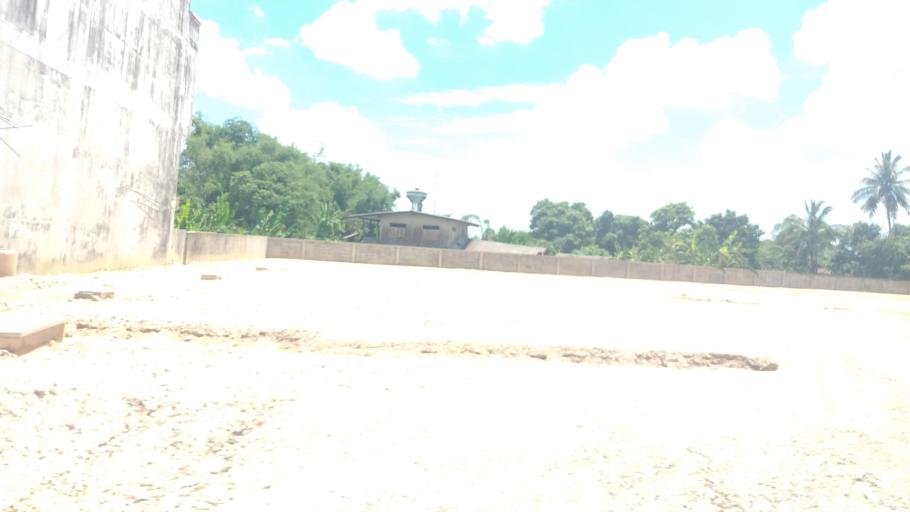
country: TH
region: Nakhon Nayok
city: Ban Na
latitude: 14.2808
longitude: 101.0666
